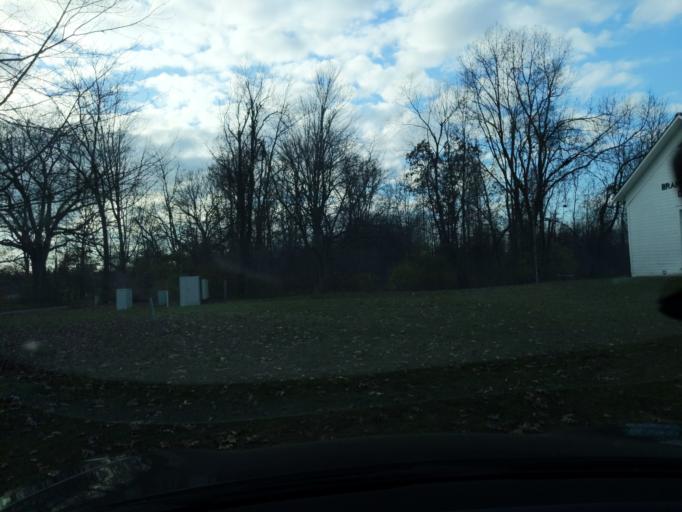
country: US
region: Michigan
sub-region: Ingham County
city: Williamston
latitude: 42.7157
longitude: -84.3250
